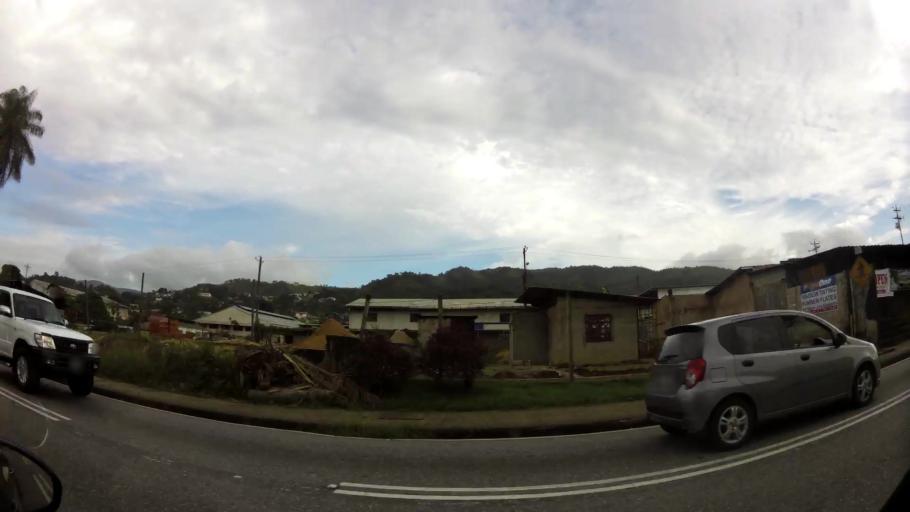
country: TT
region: Tunapuna/Piarco
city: Tunapuna
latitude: 10.6503
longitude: -61.4349
